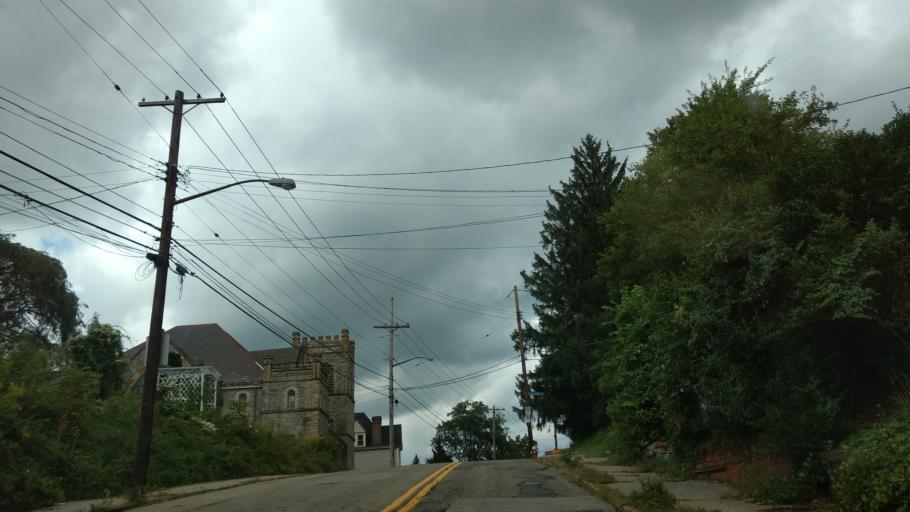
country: US
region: Pennsylvania
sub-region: Allegheny County
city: Pittsburgh
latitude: 40.4655
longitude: -80.0100
